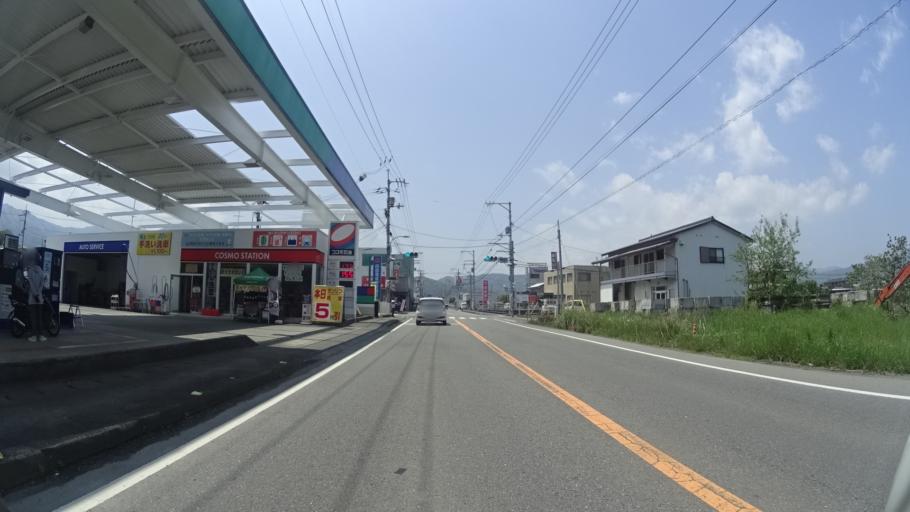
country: JP
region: Tokushima
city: Wakimachi
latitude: 34.0583
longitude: 134.2441
